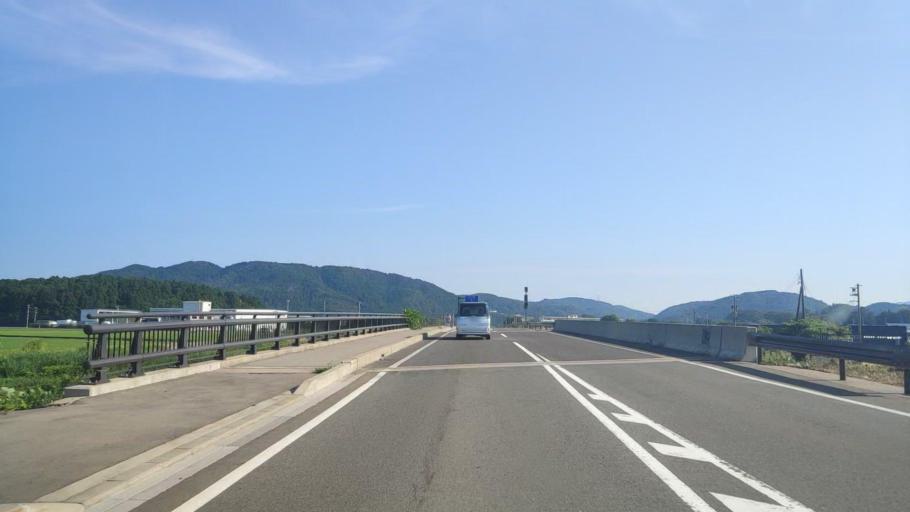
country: JP
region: Fukui
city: Maruoka
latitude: 36.1912
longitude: 136.2681
